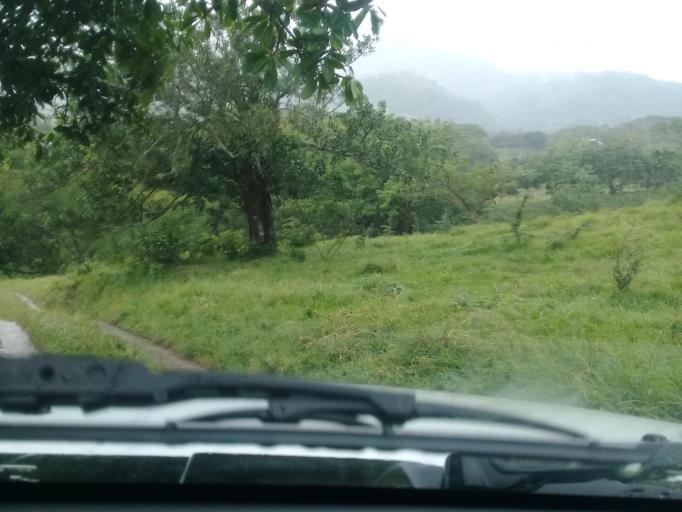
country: MX
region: Veracruz
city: Santiago Tuxtla
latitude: 18.4571
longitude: -95.3267
